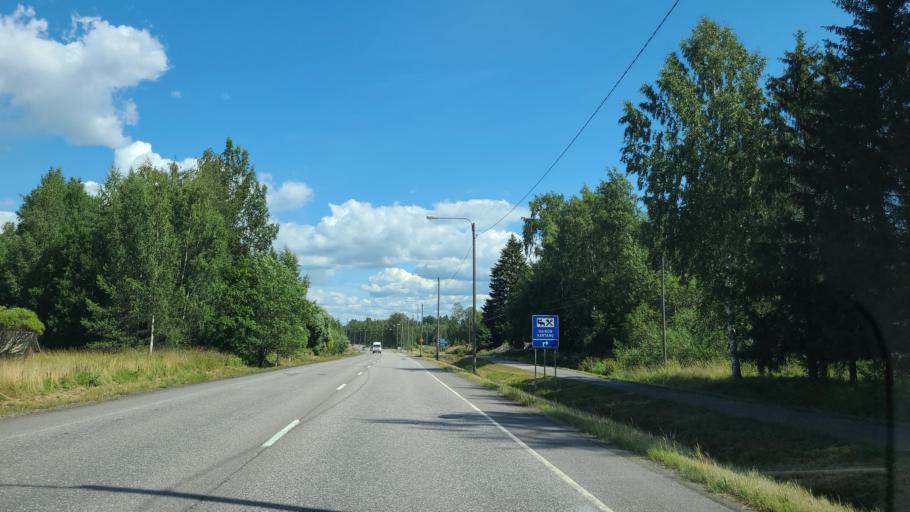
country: FI
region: Uusimaa
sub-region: Porvoo
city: Porvoo
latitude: 60.3597
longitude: 25.6076
